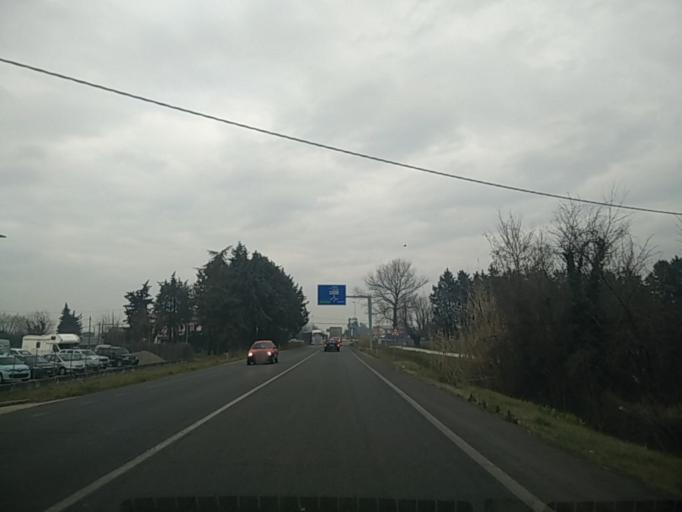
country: IT
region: Emilia-Romagna
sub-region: Provincia di Rimini
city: Santa Giustina
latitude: 44.0863
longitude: 12.4749
